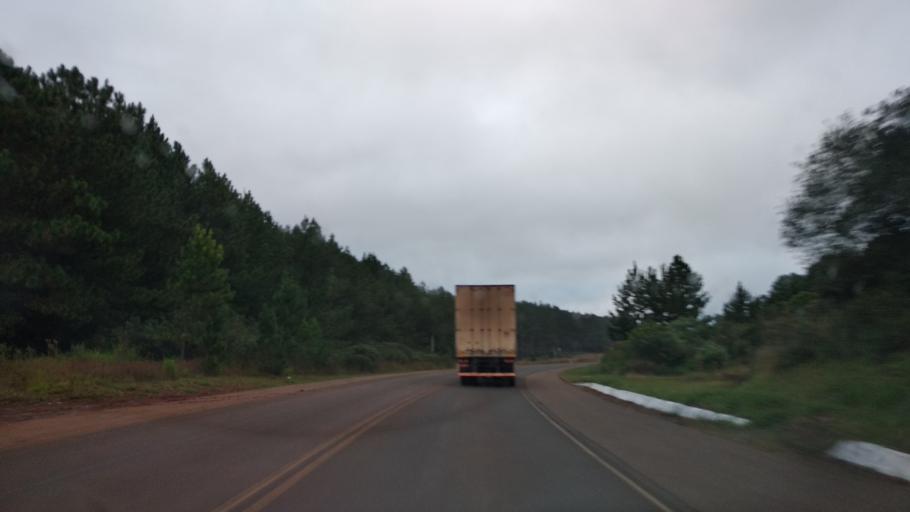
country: BR
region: Santa Catarina
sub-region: Campos Novos
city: Campos Novos
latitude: -27.3994
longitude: -51.0400
